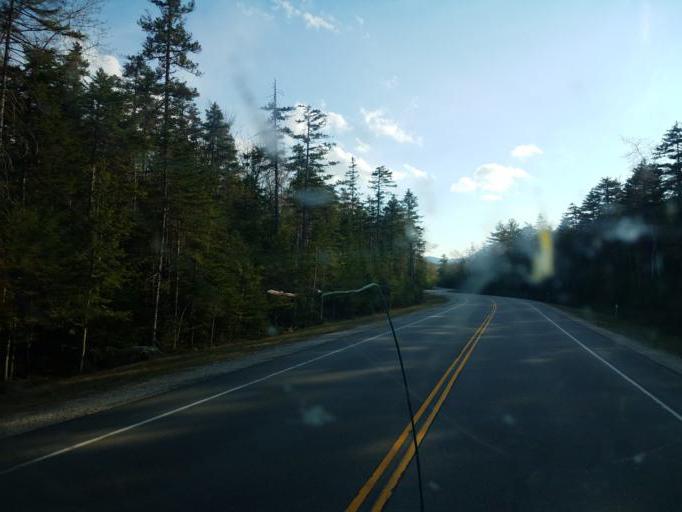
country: US
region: New Hampshire
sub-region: Carroll County
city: Tamworth
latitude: 43.9953
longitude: -71.2844
